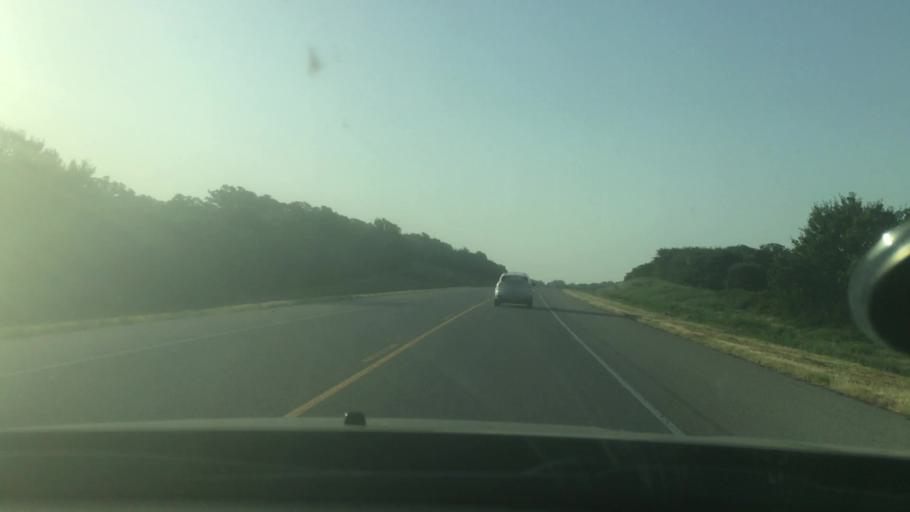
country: US
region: Oklahoma
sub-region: Pontotoc County
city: Ada
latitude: 34.6778
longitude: -96.5779
